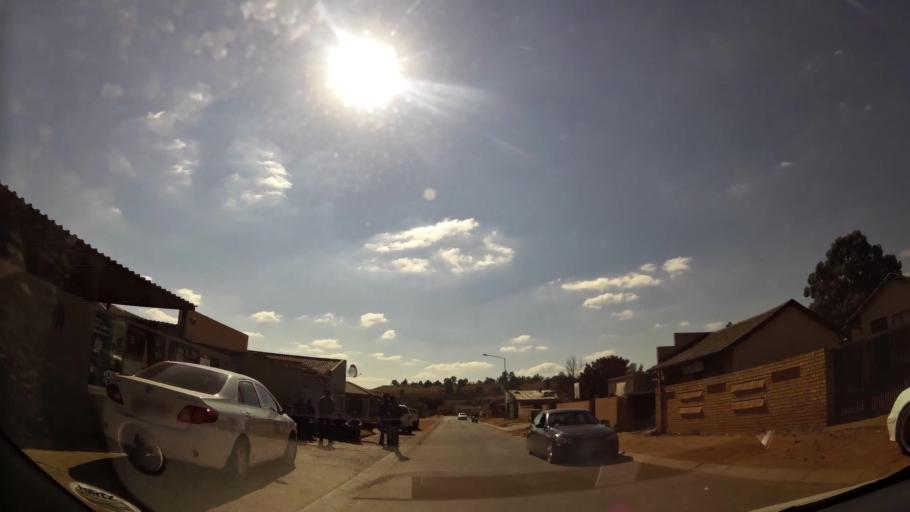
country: ZA
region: Gauteng
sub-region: West Rand District Municipality
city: Krugersdorp
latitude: -26.1488
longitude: 27.7729
